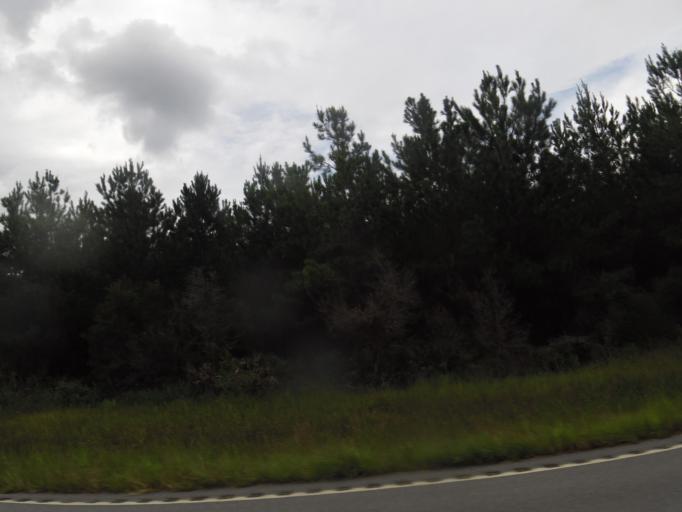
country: US
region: Florida
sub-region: Baker County
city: Macclenny
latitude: 30.5198
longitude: -82.2211
